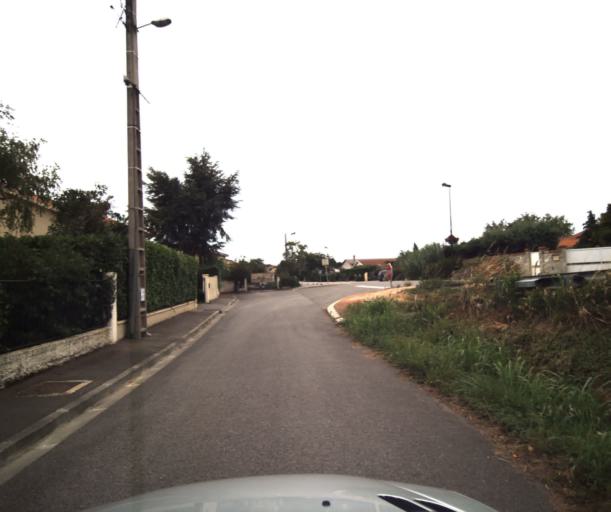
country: FR
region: Midi-Pyrenees
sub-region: Departement de la Haute-Garonne
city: Labarthe-sur-Leze
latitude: 43.4522
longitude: 1.4046
